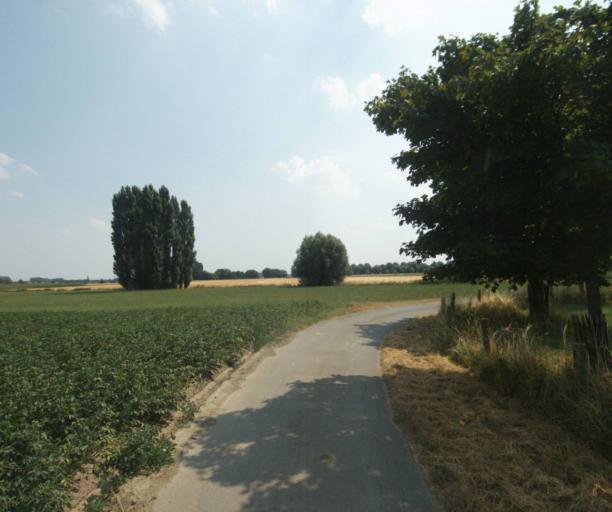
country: FR
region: Nord-Pas-de-Calais
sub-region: Departement du Nord
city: Linselles
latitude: 50.7301
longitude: 3.0398
